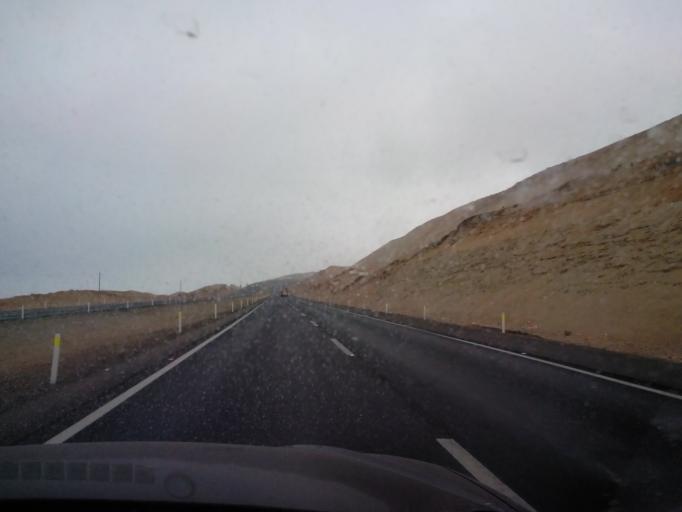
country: PE
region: Ica
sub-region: Provincia de Chincha
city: San Pedro
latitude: -13.3076
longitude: -76.2514
